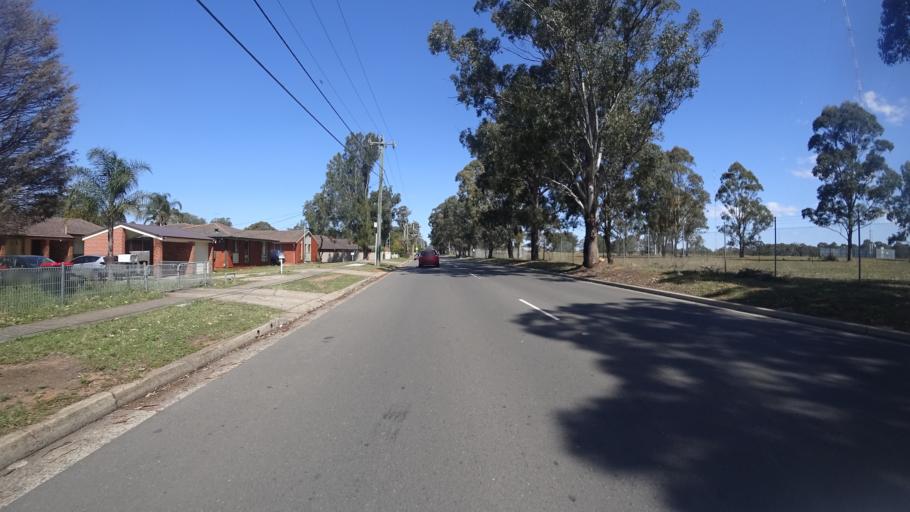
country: AU
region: New South Wales
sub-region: Liverpool
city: Miller
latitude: -33.9414
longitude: 150.8889
